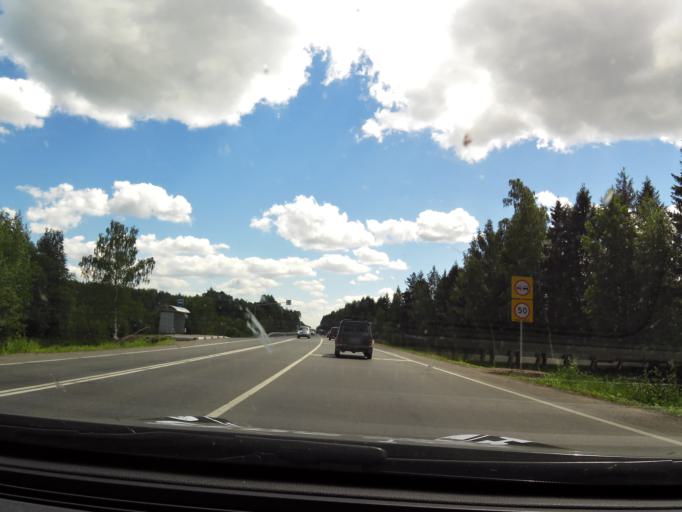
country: RU
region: Vologda
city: Molochnoye
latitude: 59.2766
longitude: 39.7149
